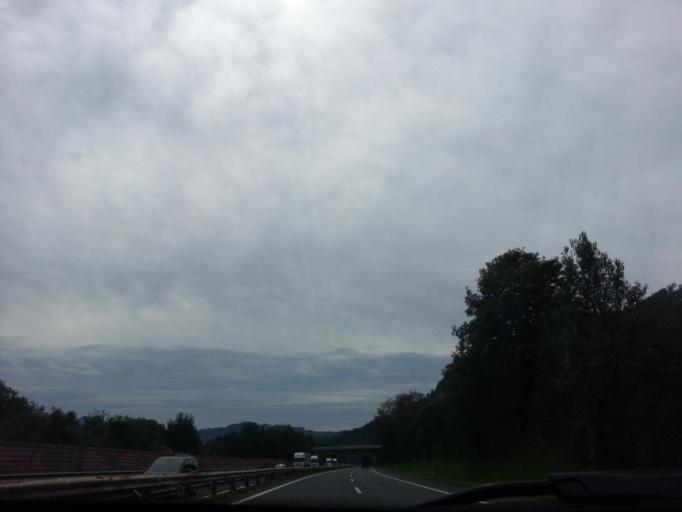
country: AT
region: Styria
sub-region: Politischer Bezirk Graz-Umgebung
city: Deutschfeistritz
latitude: 47.2157
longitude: 15.3048
